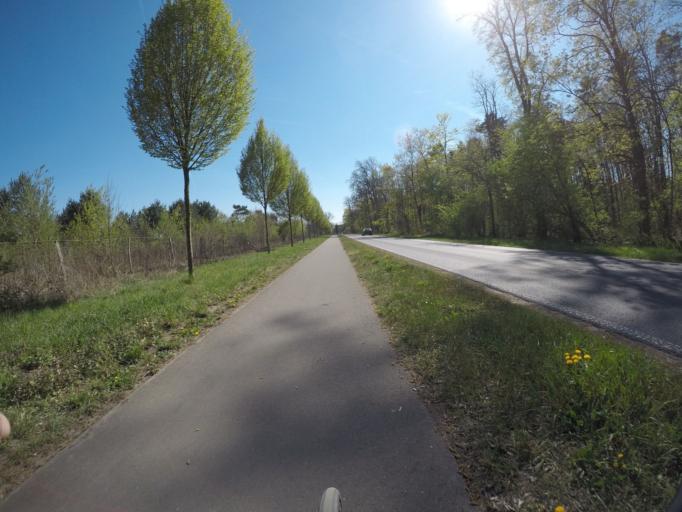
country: DE
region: Brandenburg
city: Rehfelde
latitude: 52.5379
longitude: 13.9352
